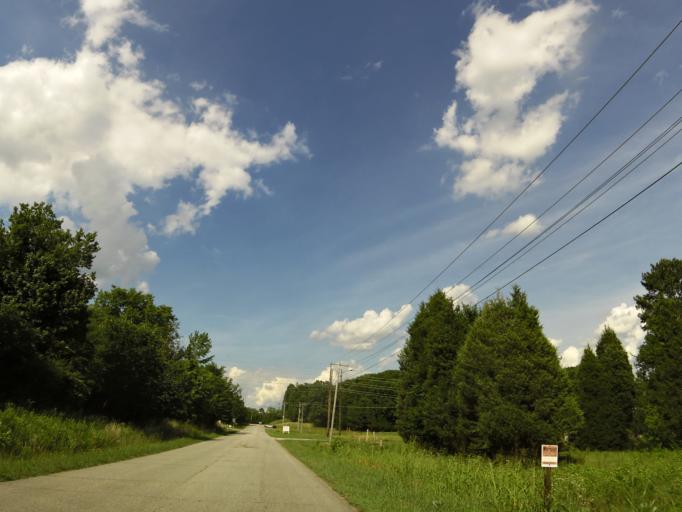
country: US
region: Tennessee
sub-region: Carroll County
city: Huntingdon
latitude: 36.0209
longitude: -88.3806
